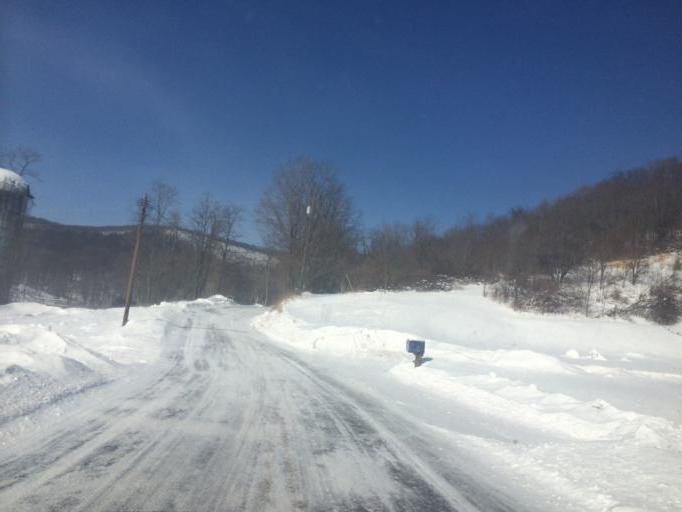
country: US
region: Pennsylvania
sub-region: Centre County
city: Stormstown
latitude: 40.8588
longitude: -78.0232
